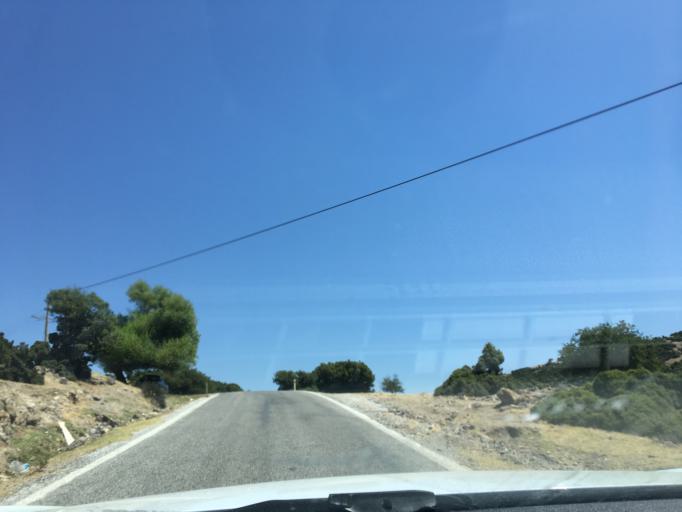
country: TR
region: Canakkale
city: Gulpinar
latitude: 39.4905
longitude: 26.1509
